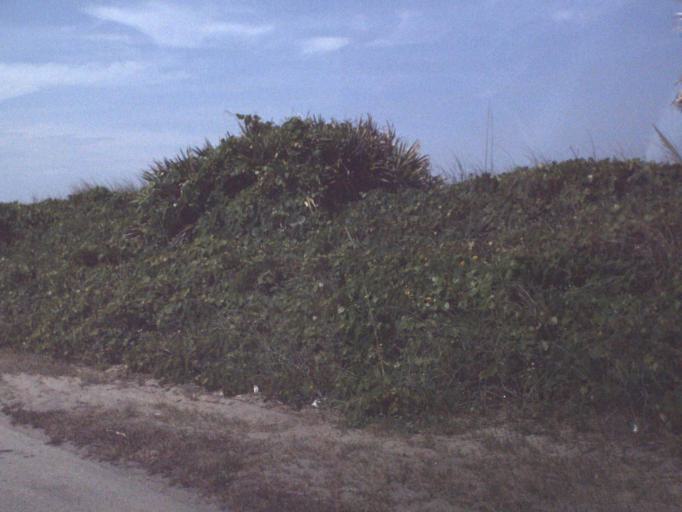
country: US
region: Florida
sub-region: Saint Johns County
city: Villano Beach
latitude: 29.9314
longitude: -81.2972
